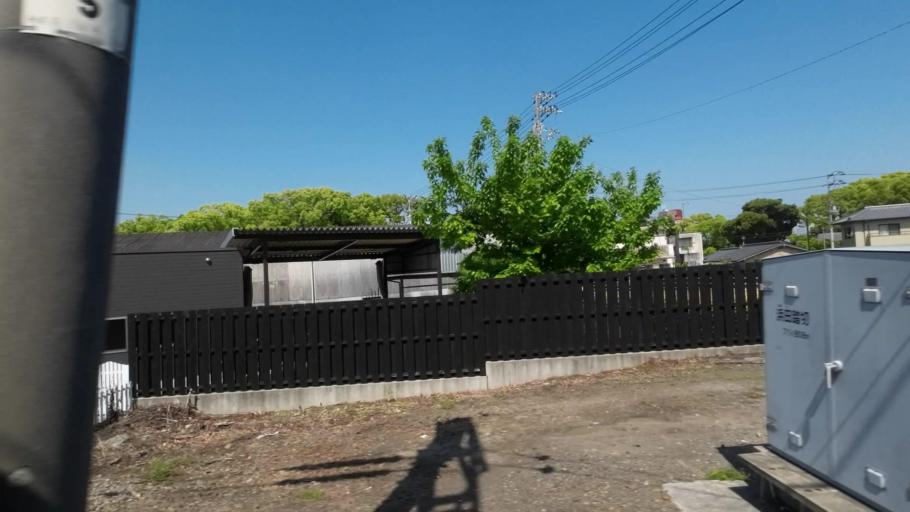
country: JP
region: Ehime
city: Kawanoecho
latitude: 34.0172
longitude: 133.5767
